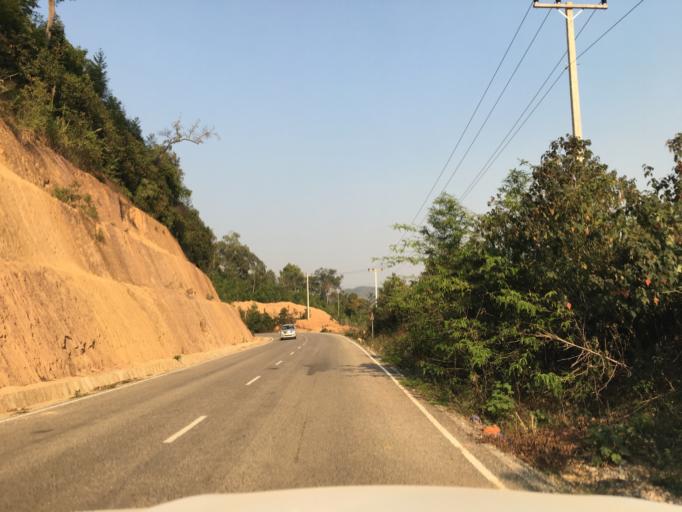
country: LA
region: Houaphan
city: Xam Nua
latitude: 20.5870
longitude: 104.0597
